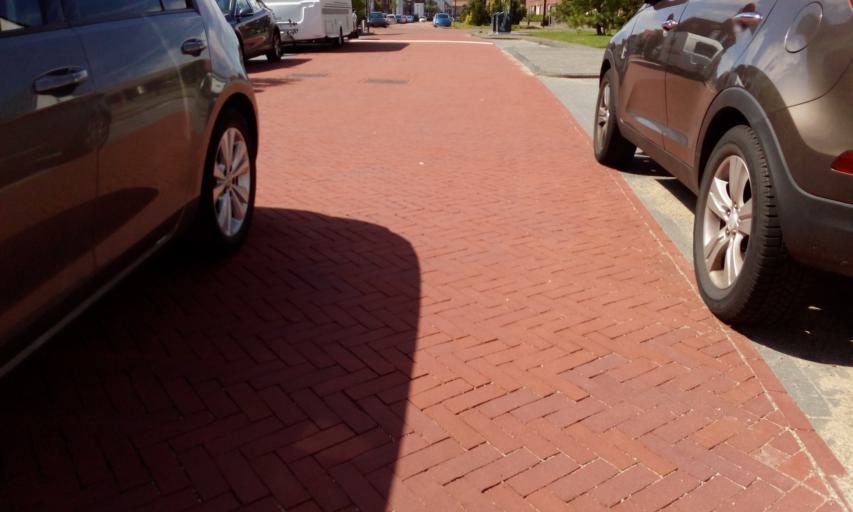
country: NL
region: South Holland
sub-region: Gemeente Rijswijk
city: Rijswijk
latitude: 52.0359
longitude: 4.2936
